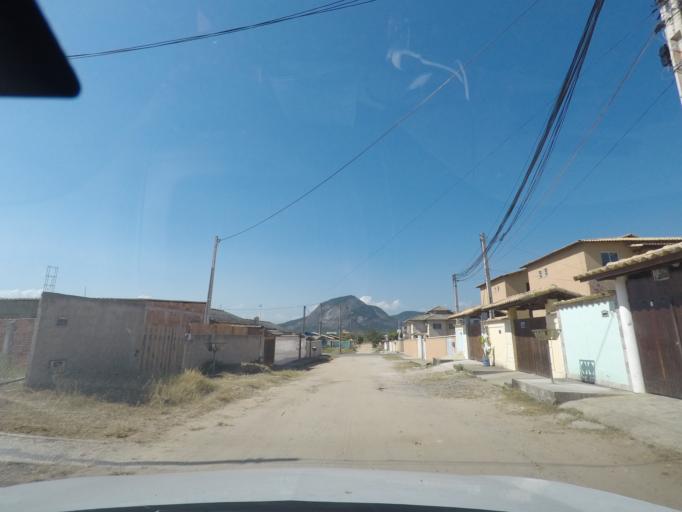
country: BR
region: Rio de Janeiro
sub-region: Marica
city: Marica
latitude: -22.9674
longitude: -42.9092
